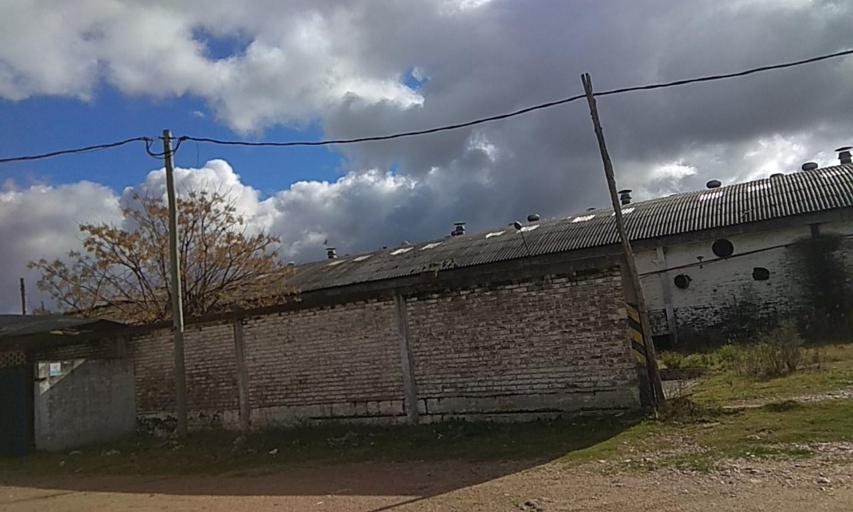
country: UY
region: Florida
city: Florida
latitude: -34.1114
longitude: -56.2230
